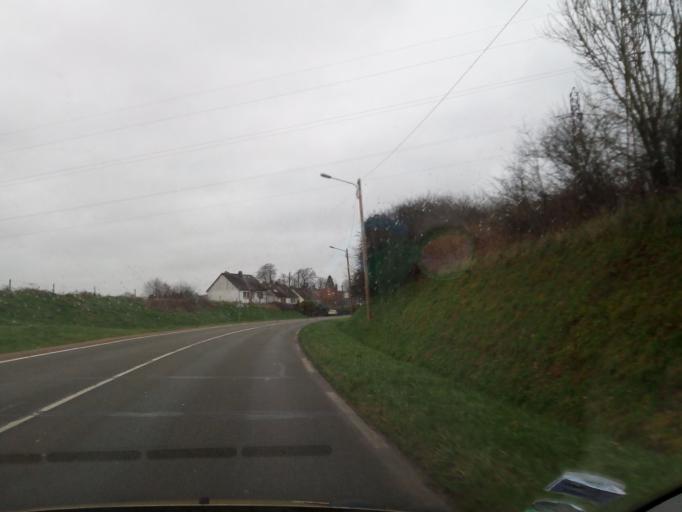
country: FR
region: Haute-Normandie
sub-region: Departement de la Seine-Maritime
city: Yvetot
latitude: 49.6090
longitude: 0.7426
